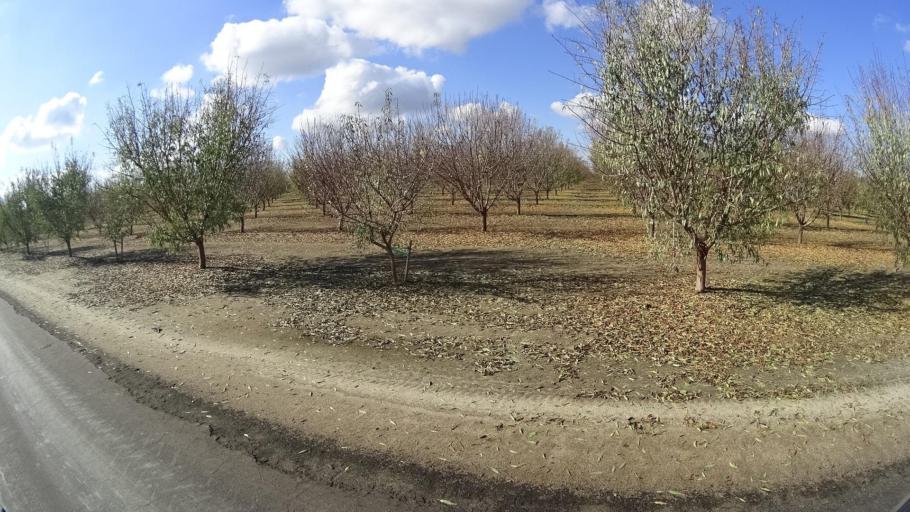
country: US
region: California
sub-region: Kern County
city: McFarland
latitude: 35.6434
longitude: -119.2322
